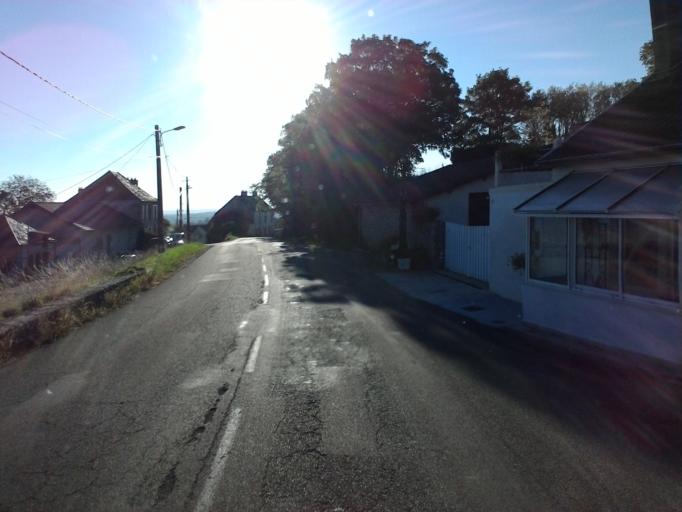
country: FR
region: Bourgogne
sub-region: Departement de la Cote-d'Or
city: Saulieu
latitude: 47.2752
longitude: 4.2338
